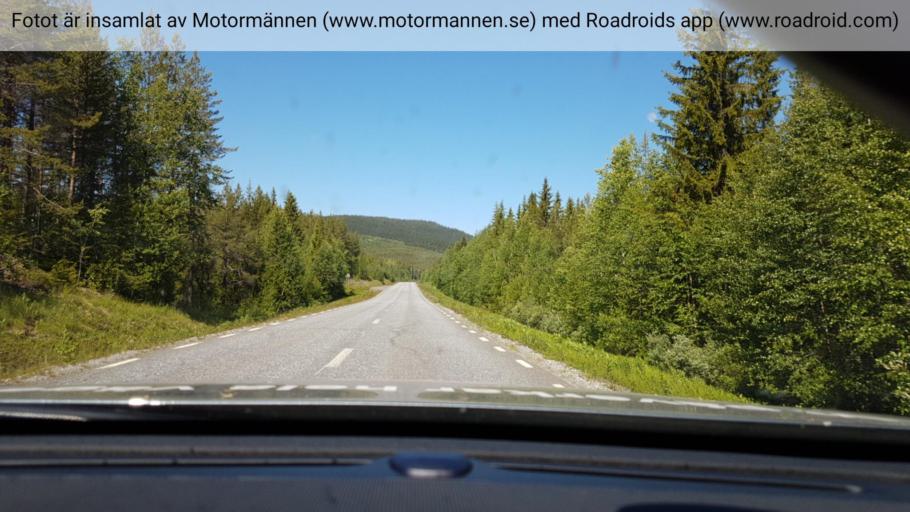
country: SE
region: Vaesterbotten
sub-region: Vilhelmina Kommun
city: Sjoberg
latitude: 64.8897
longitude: 15.8621
